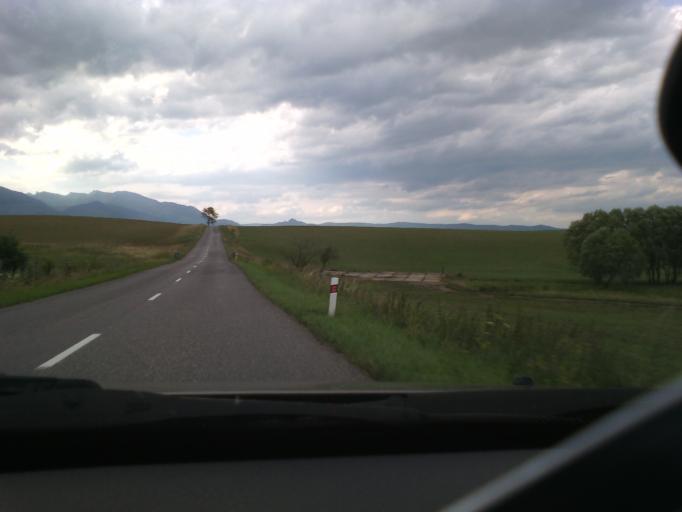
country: SK
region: Presovsky
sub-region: Okres Presov
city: Kezmarok
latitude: 49.0904
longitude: 20.3996
